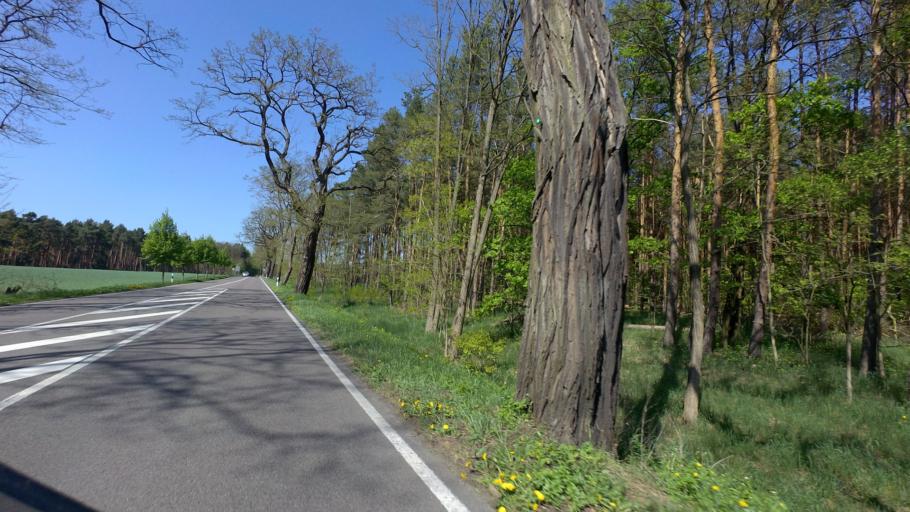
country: DE
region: Brandenburg
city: Lieberose
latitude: 52.0257
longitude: 14.3047
